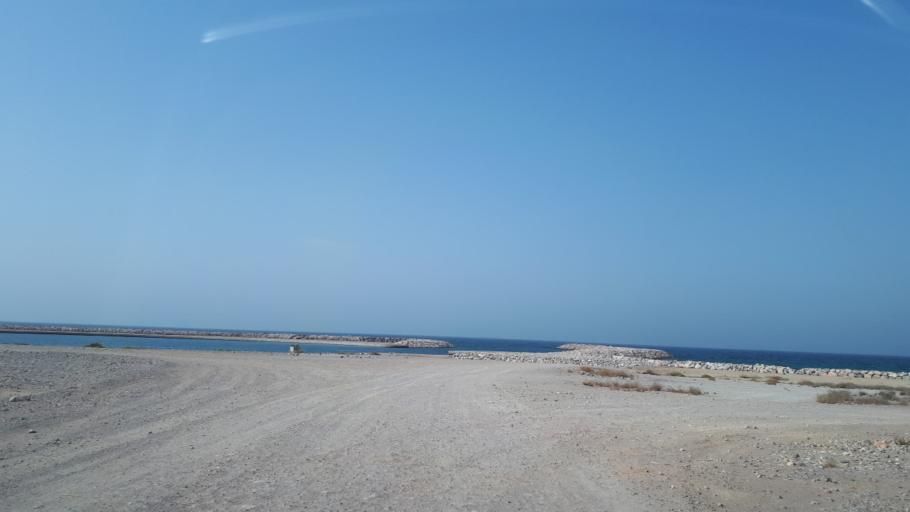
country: OM
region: Muhafazat Masqat
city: Muscat
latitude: 23.5427
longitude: 58.6693
